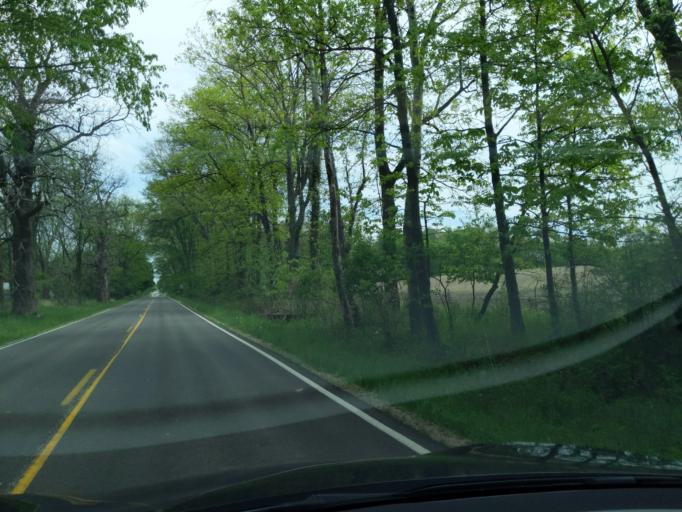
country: US
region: Michigan
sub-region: Ingham County
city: Stockbridge
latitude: 42.4684
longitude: -84.1686
